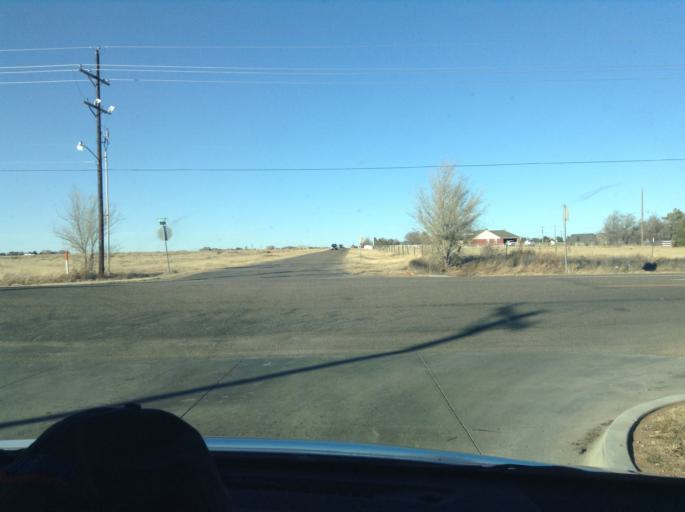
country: US
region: Texas
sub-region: Randall County
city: Canyon
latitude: 34.9994
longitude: -101.9305
